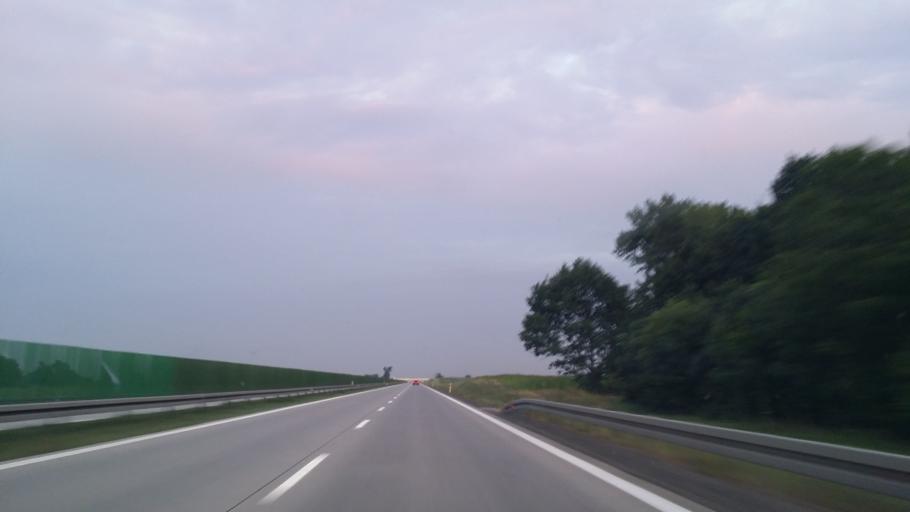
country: PL
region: Lower Silesian Voivodeship
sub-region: Powiat sredzki
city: Udanin
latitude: 51.1210
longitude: 16.3728
